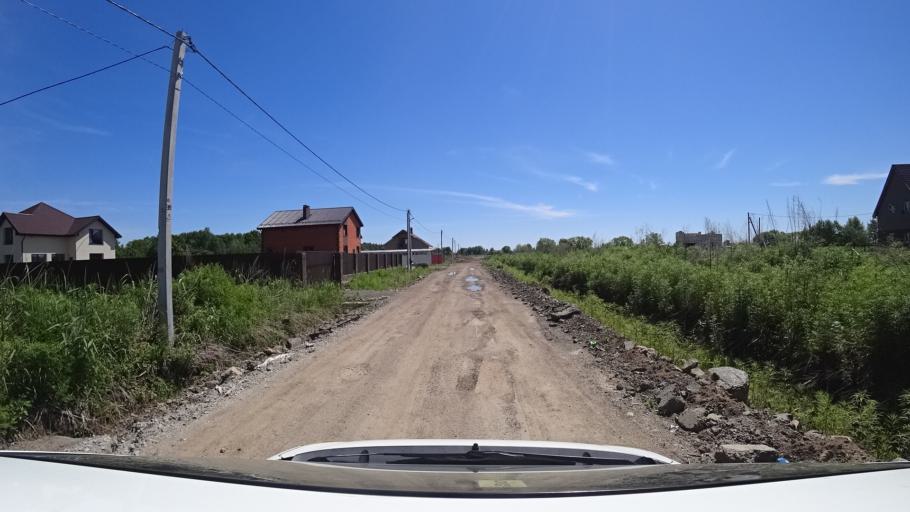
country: RU
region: Khabarovsk Krai
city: Topolevo
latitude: 48.5154
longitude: 135.1982
